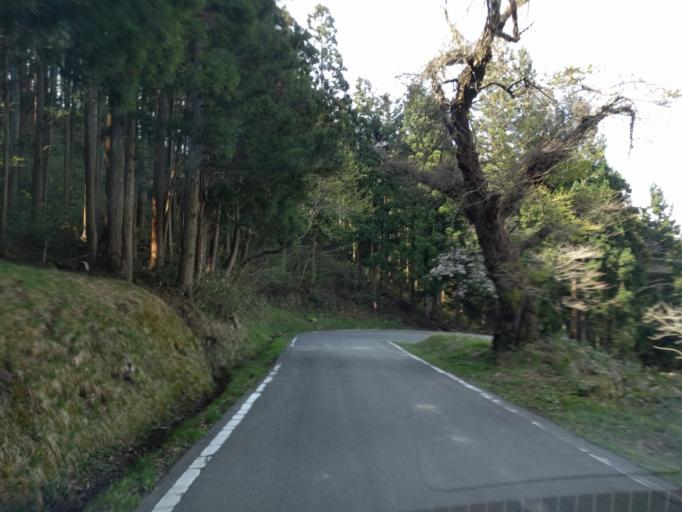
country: JP
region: Fukushima
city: Inawashiro
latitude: 37.5189
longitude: 140.0318
